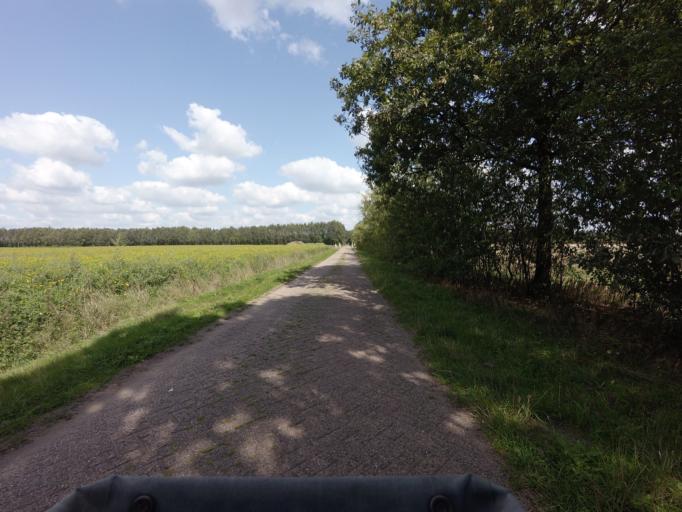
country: NL
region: Drenthe
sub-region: Gemeente Westerveld
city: Dwingeloo
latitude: 52.8792
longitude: 6.3838
